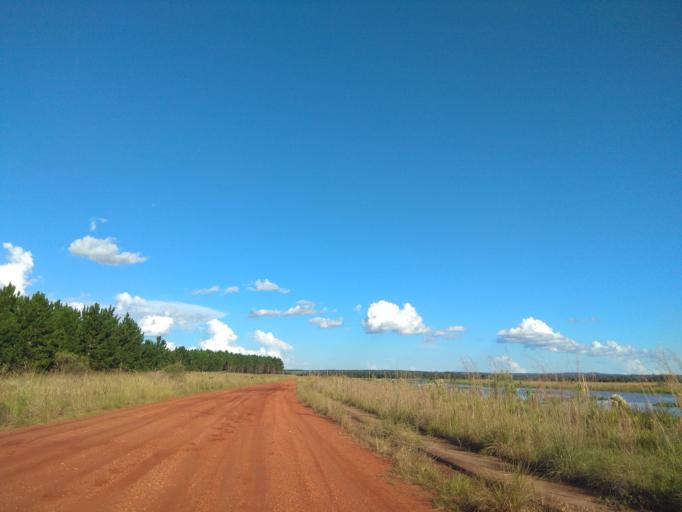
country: AR
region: Misiones
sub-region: Departamento de Candelaria
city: Candelaria
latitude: -27.4914
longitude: -55.7777
